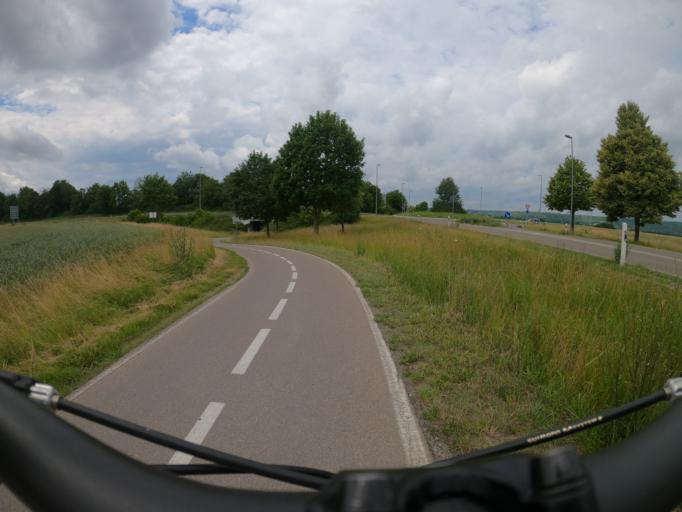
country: DE
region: Bavaria
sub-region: Swabia
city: Neu-Ulm
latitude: 48.4144
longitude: 10.0573
